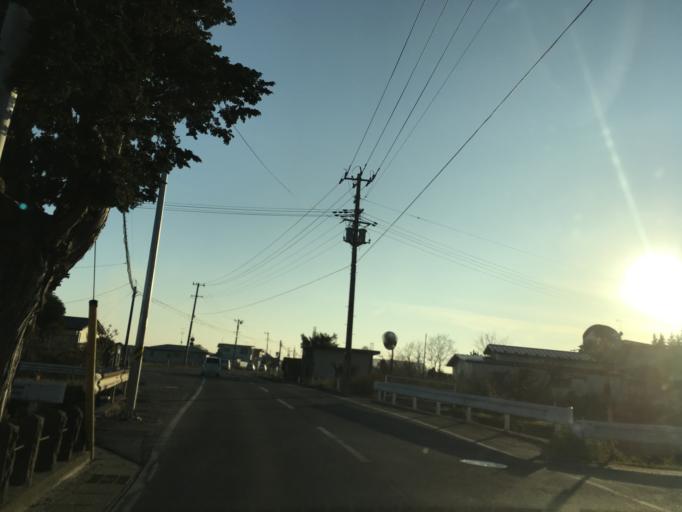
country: JP
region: Miyagi
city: Wakuya
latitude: 38.7171
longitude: 141.2101
